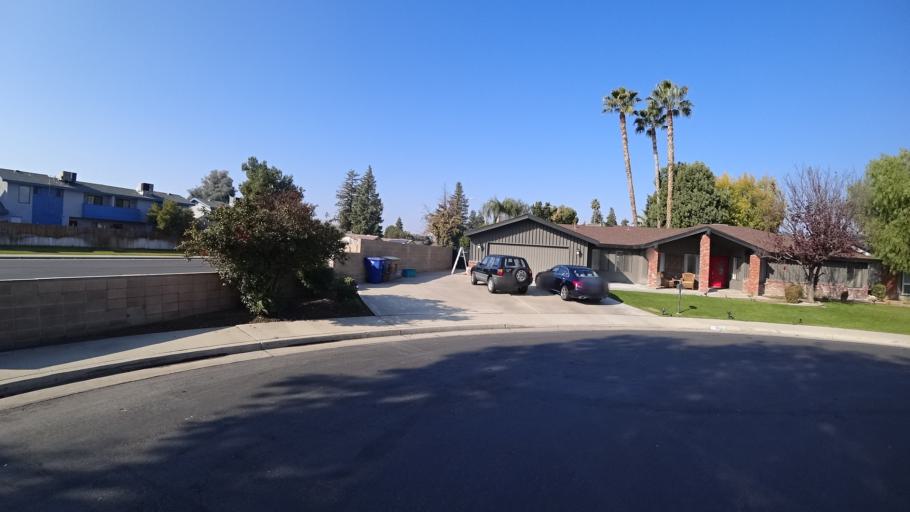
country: US
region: California
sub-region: Kern County
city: Greenacres
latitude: 35.3254
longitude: -119.0870
